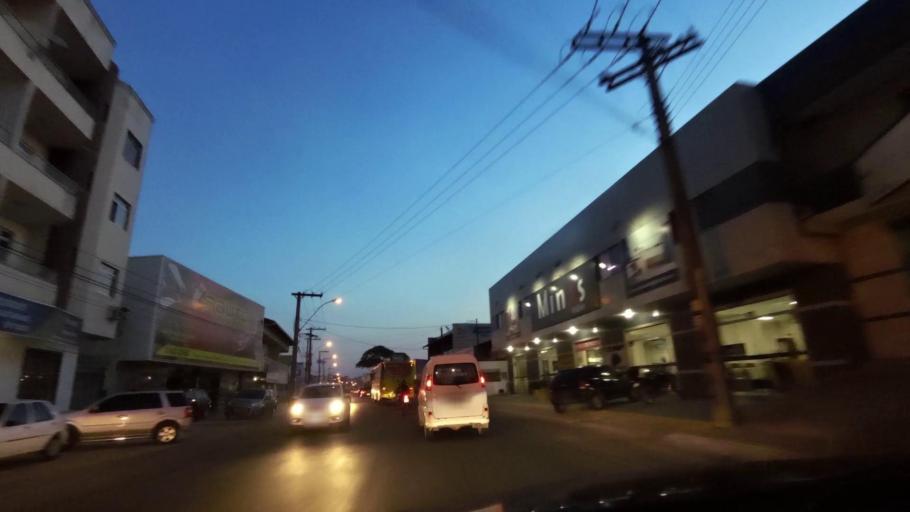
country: BR
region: Espirito Santo
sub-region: Guarapari
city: Guarapari
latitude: -20.6487
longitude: -40.4921
